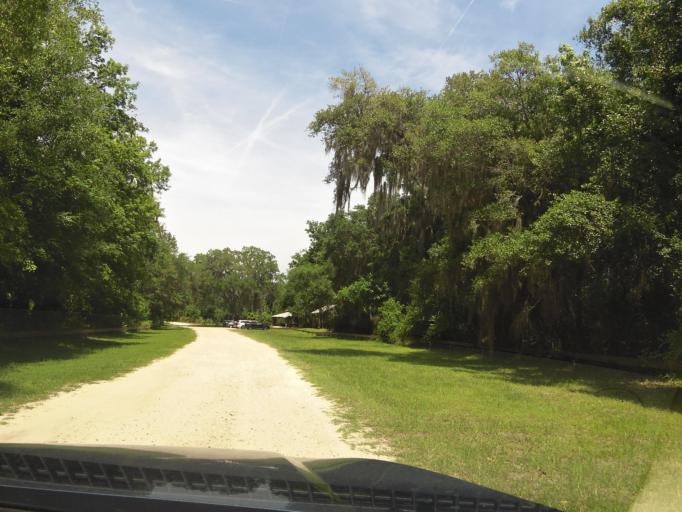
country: US
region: Florida
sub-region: Duval County
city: Atlantic Beach
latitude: 30.4853
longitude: -81.4904
